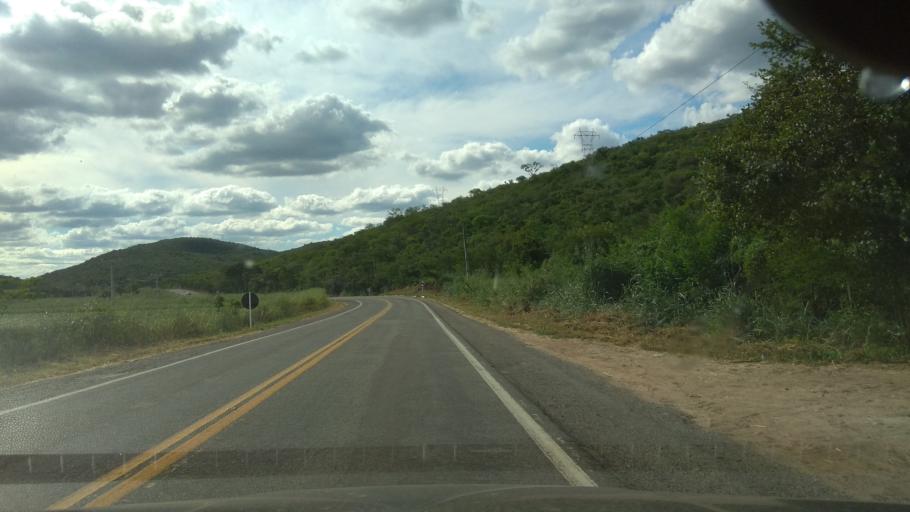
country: BR
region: Bahia
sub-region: Jequie
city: Jequie
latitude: -13.8995
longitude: -40.0190
